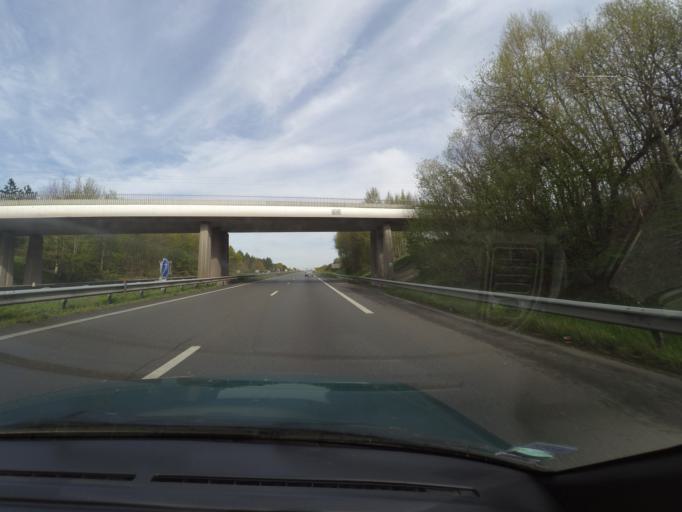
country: FR
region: Pays de la Loire
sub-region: Departement de la Loire-Atlantique
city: Le Bignon
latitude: 47.1188
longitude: -1.4955
